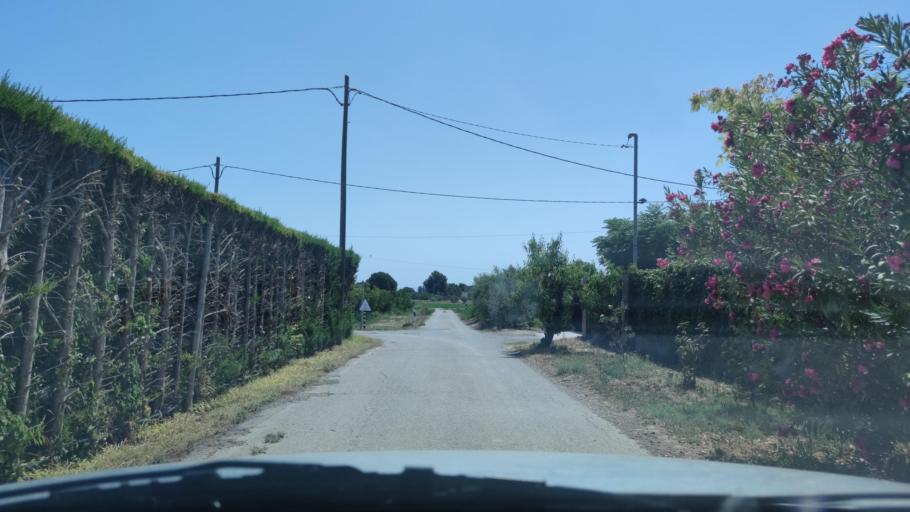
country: ES
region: Catalonia
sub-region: Provincia de Lleida
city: Torrefarrera
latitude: 41.6482
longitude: 0.5867
